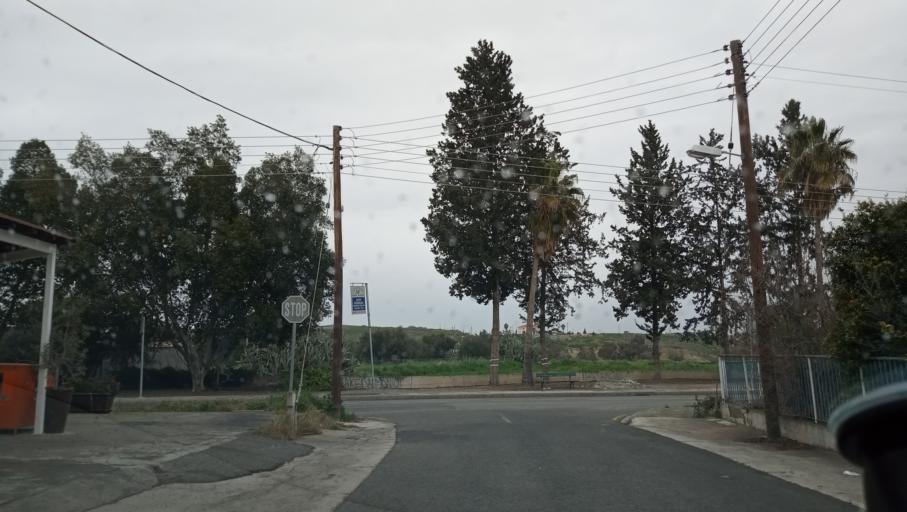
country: CY
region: Lefkosia
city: Kato Deftera
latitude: 35.0862
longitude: 33.2803
